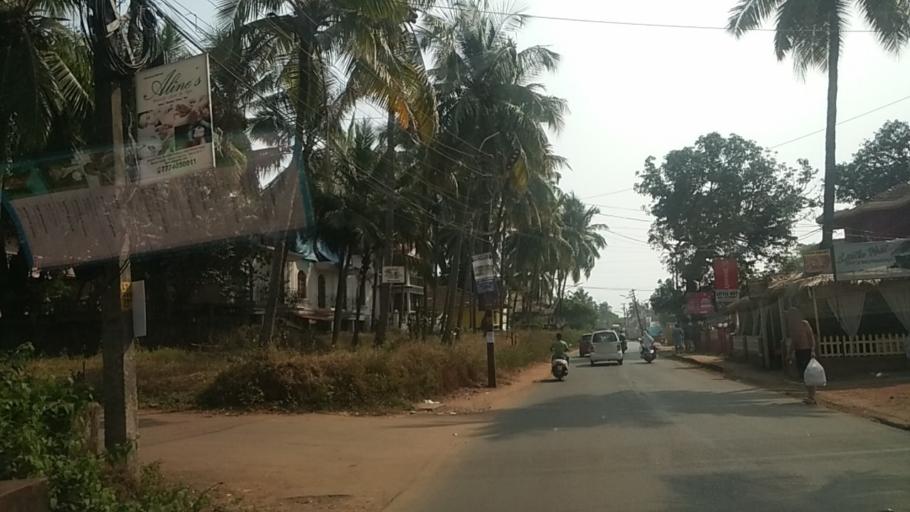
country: IN
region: Goa
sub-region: North Goa
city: Candolim
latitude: 15.5223
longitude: 73.7671
